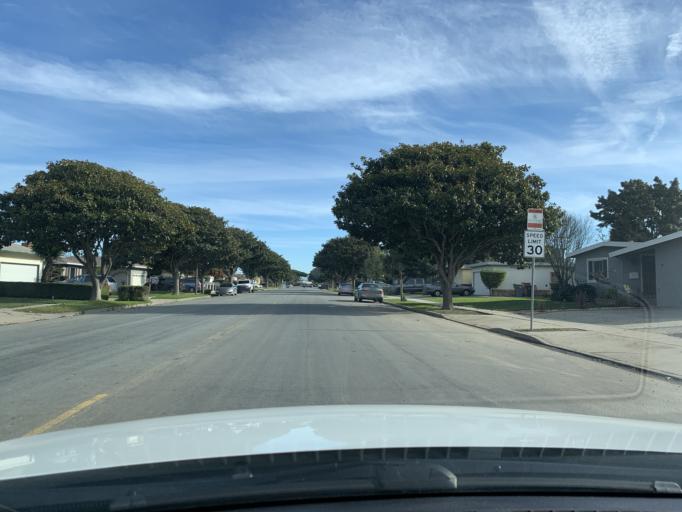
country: US
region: California
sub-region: Monterey County
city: Salinas
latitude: 36.6763
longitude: -121.6764
